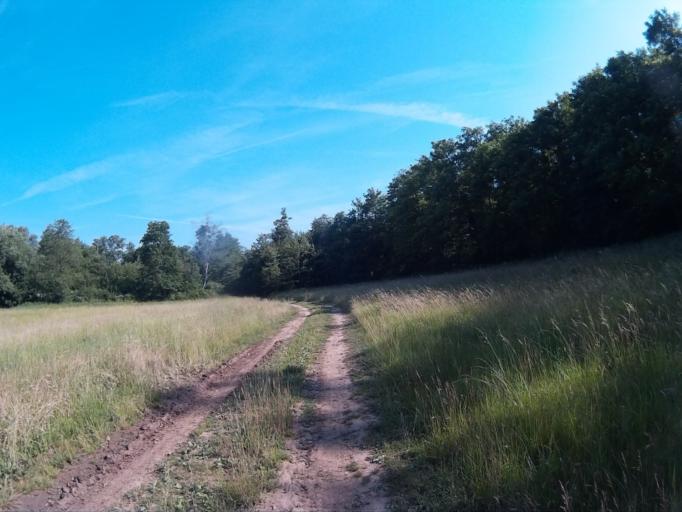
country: AT
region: Burgenland
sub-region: Politischer Bezirk Gussing
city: Heiligenbrunn
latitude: 46.9362
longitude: 16.4709
